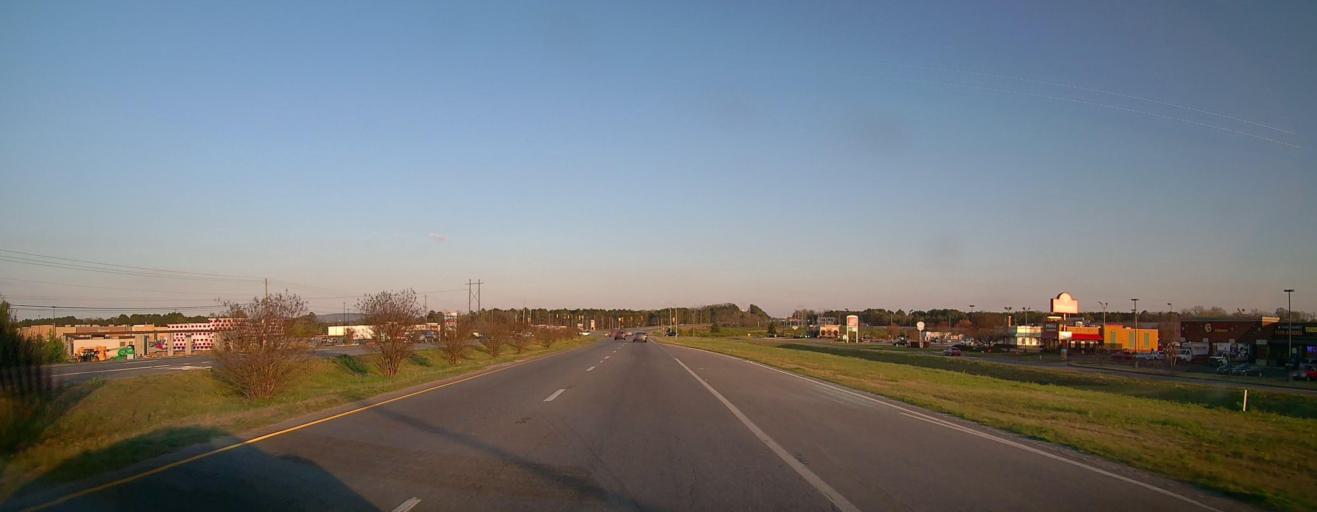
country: US
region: Alabama
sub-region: Talladega County
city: Mignon
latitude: 33.1750
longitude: -86.2897
